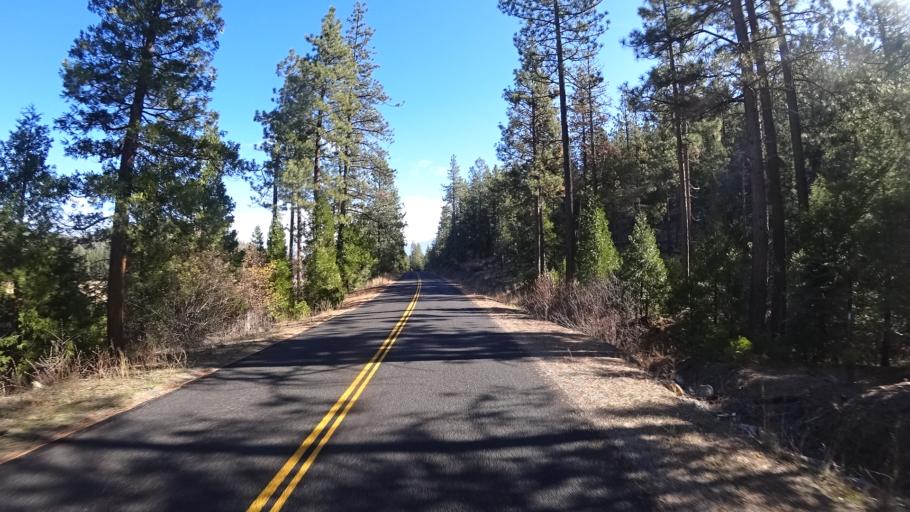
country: US
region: California
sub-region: Siskiyou County
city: Weed
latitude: 41.4323
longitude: -122.4893
